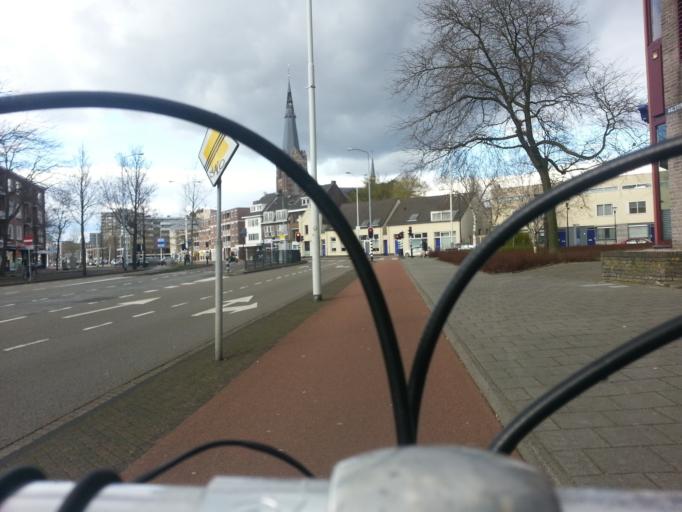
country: NL
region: North Brabant
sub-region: Gemeente Eindhoven
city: Villapark
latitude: 51.4276
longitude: 5.4870
